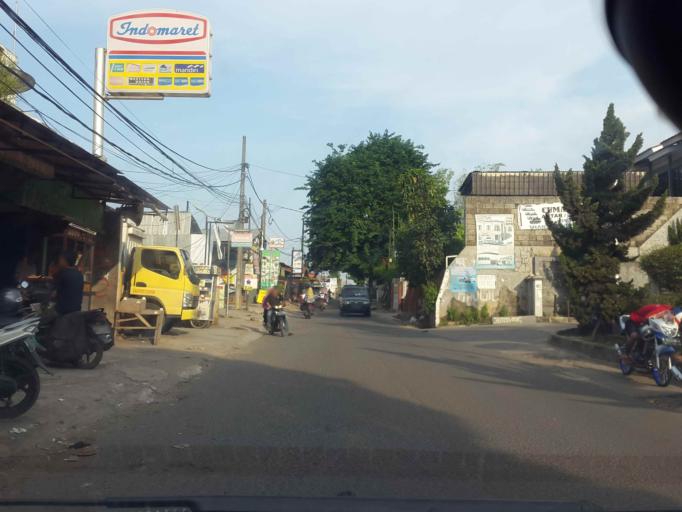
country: ID
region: West Java
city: Ciputat
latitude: -6.2444
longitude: 106.6942
